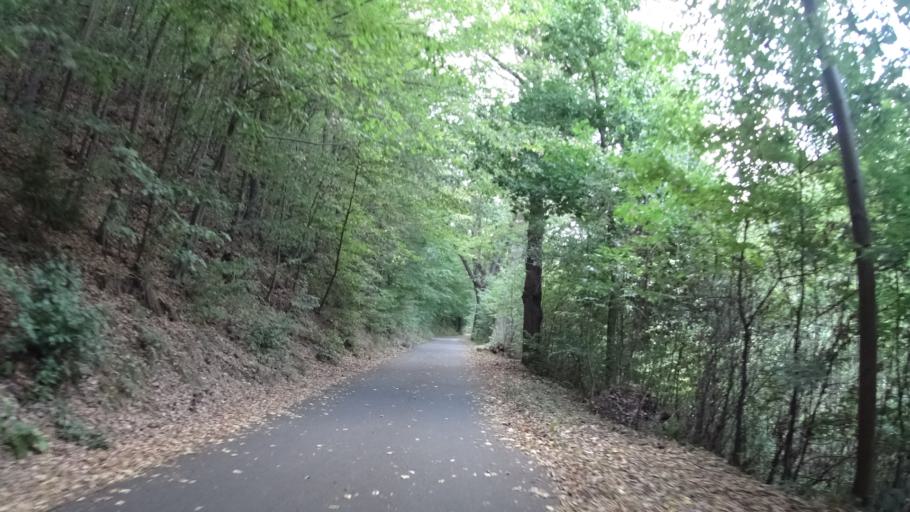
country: DE
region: Saxony
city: Ostritz
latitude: 50.9948
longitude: 14.9167
